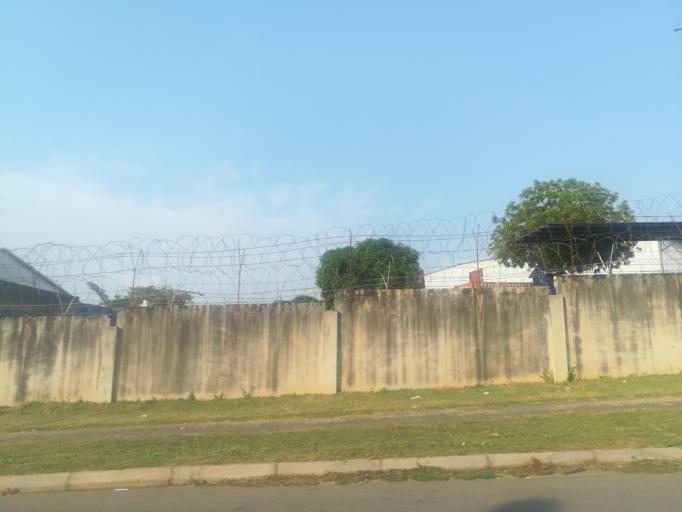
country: NG
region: Abuja Federal Capital Territory
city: Abuja
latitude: 9.0609
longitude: 7.4474
